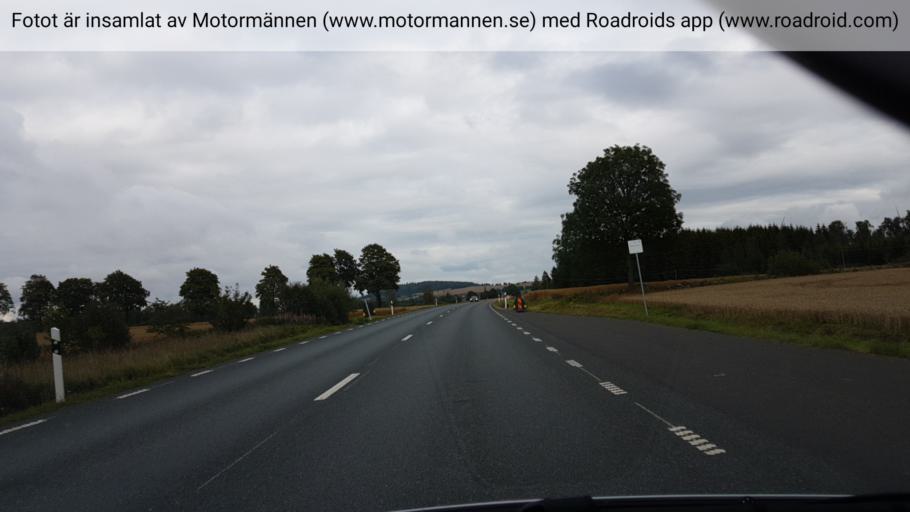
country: SE
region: Vaestra Goetaland
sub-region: Falkopings Kommun
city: Akarp
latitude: 58.1252
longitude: 13.7172
